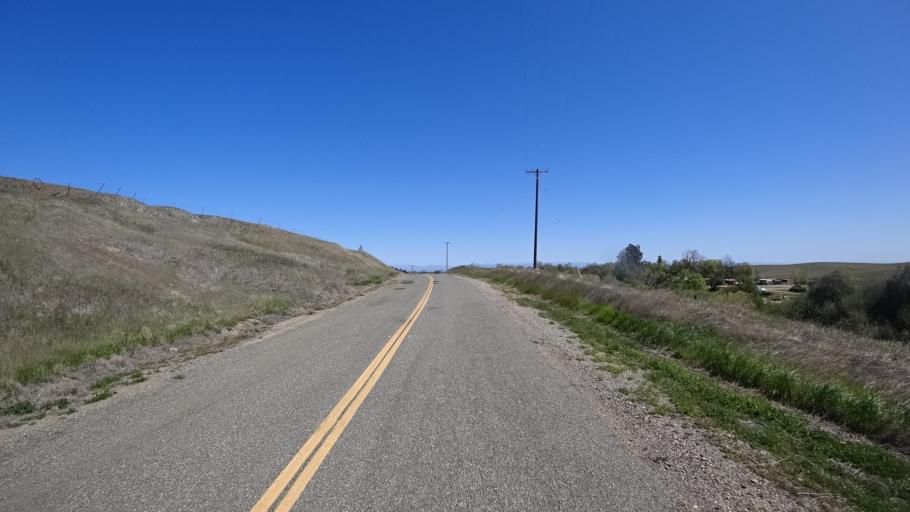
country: US
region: California
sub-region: Glenn County
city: Orland
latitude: 39.7651
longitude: -122.3323
